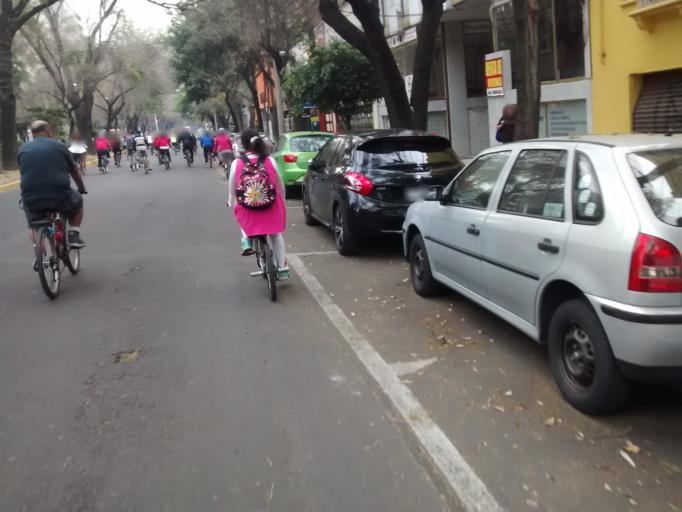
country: MX
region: Mexico City
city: Benito Juarez
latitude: 19.4182
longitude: -99.1737
